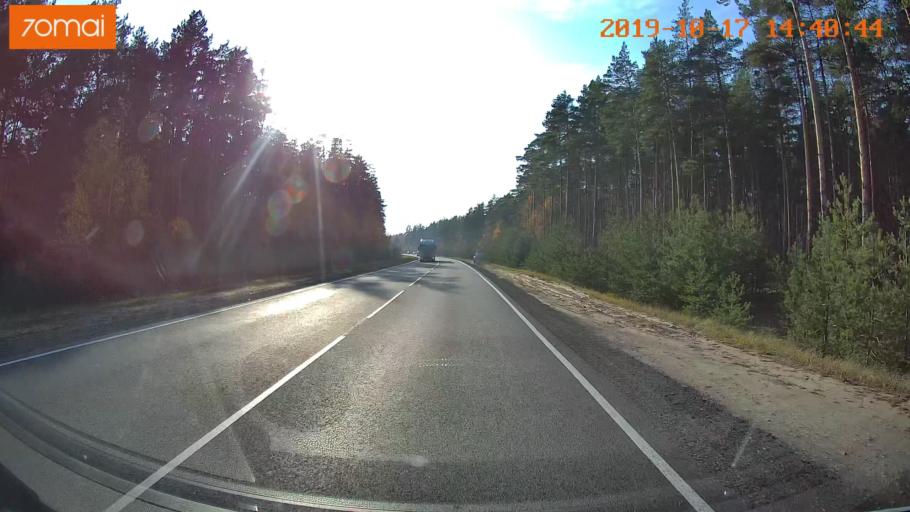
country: RU
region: Rjazan
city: Solotcha
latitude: 54.8531
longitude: 39.9508
